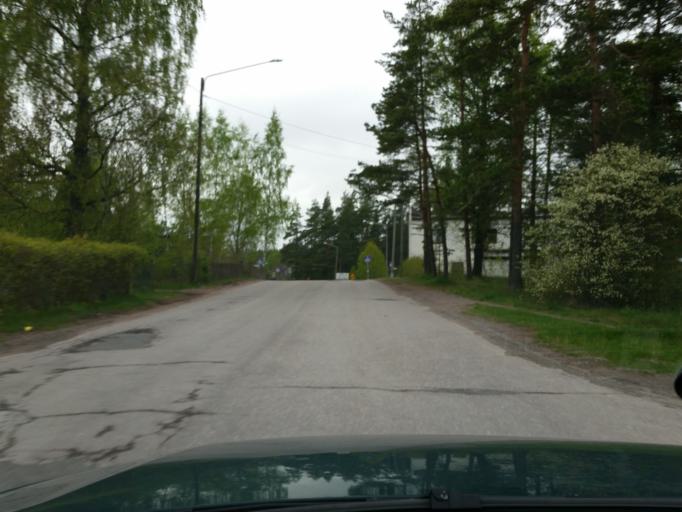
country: FI
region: Uusimaa
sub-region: Raaseporin
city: Inga
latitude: 60.1371
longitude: 23.8653
